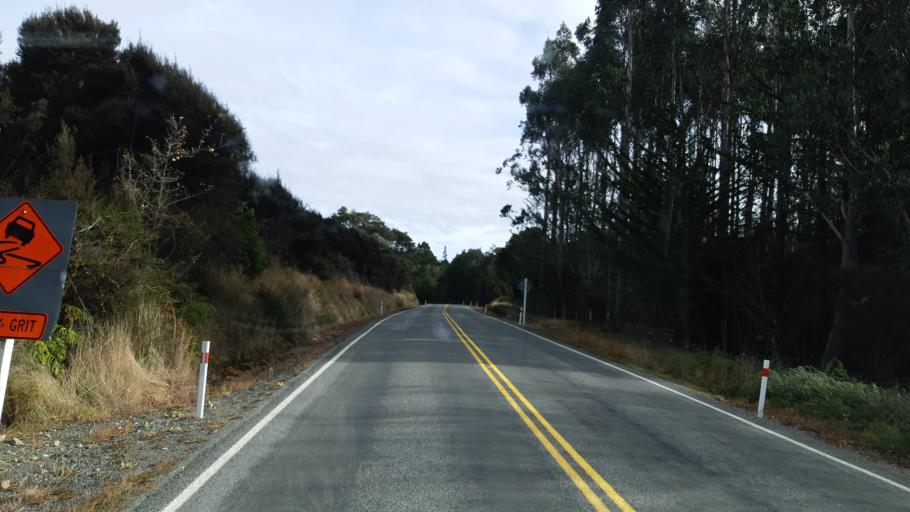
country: NZ
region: Tasman
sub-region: Tasman District
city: Wakefield
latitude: -41.7774
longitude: 172.9180
